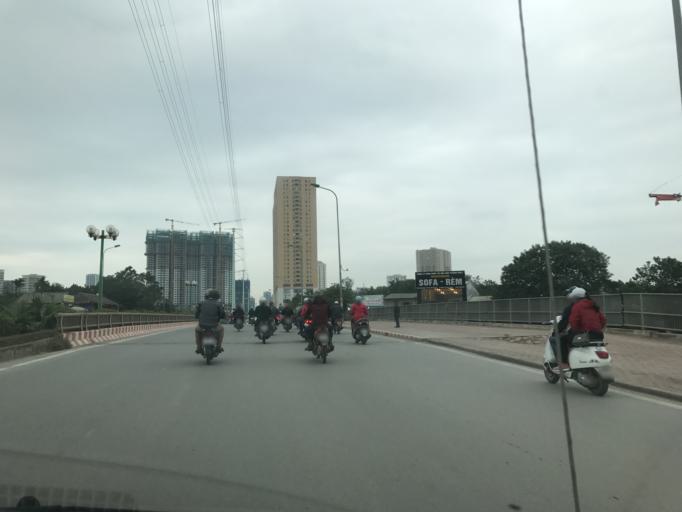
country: VN
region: Ha Noi
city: Ha Dong
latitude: 20.9883
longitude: 105.7801
